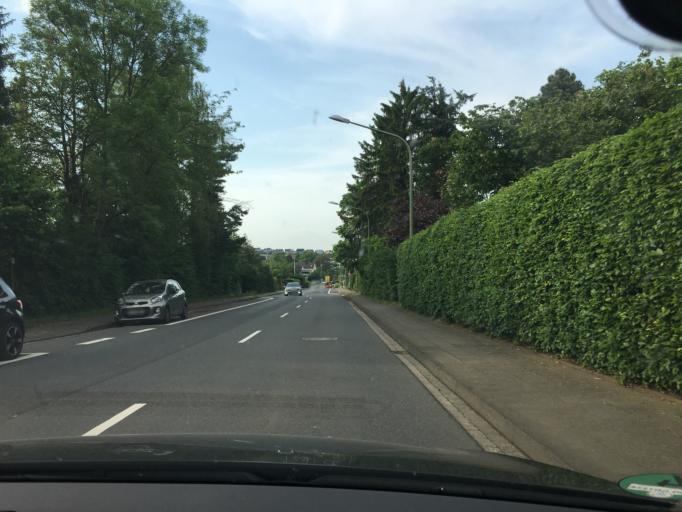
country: DE
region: North Rhine-Westphalia
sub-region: Regierungsbezirk Koln
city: Nideggen
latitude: 50.6893
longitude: 6.4852
